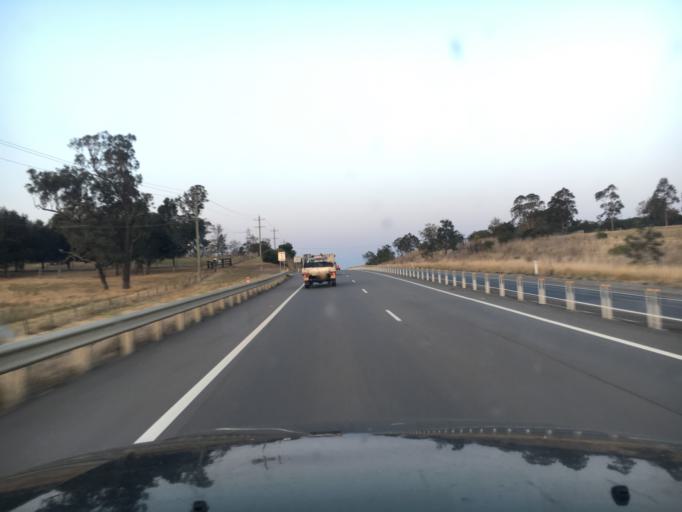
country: AU
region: New South Wales
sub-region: Cessnock
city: Greta
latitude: -32.7055
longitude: 151.4334
